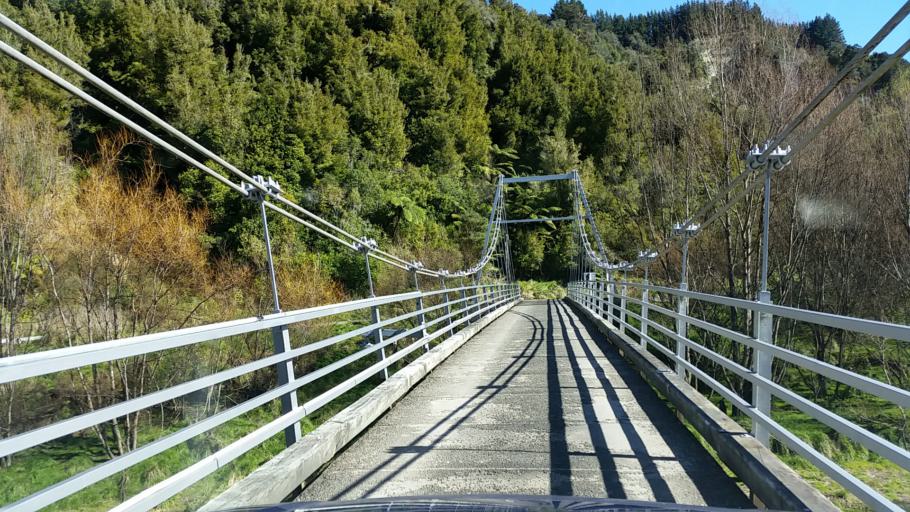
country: NZ
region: Manawatu-Wanganui
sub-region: Wanganui District
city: Wanganui
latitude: -39.6130
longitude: 174.8398
